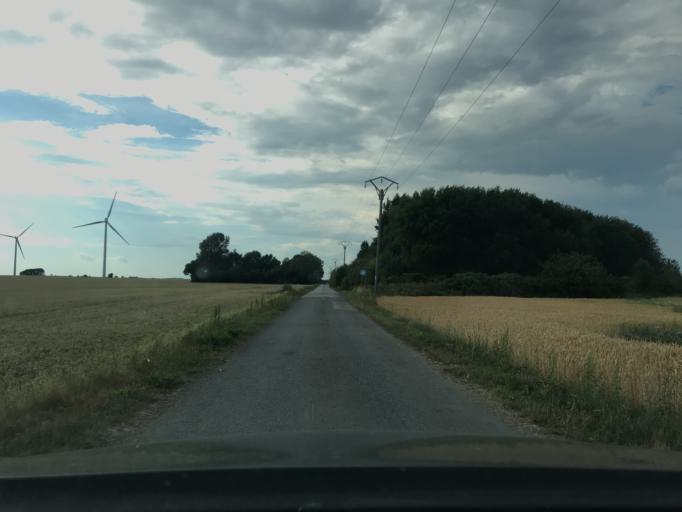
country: SE
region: Skane
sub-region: Simrishamns Kommun
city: Kivik
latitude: 55.5279
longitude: 14.1635
